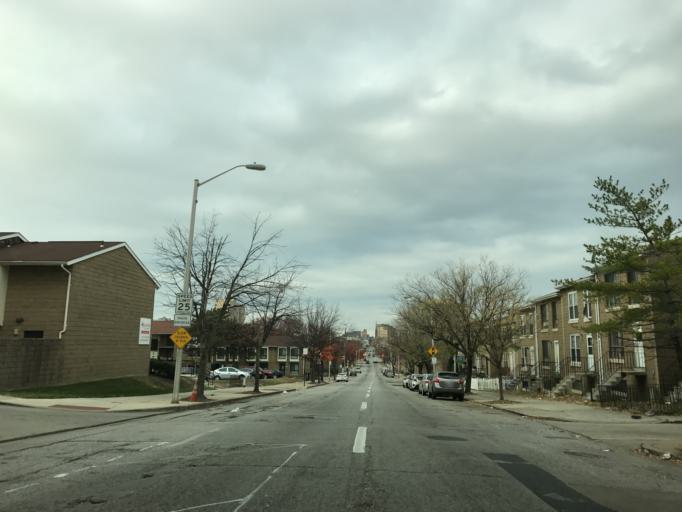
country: US
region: Maryland
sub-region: City of Baltimore
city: Baltimore
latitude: 39.2994
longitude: -76.5947
